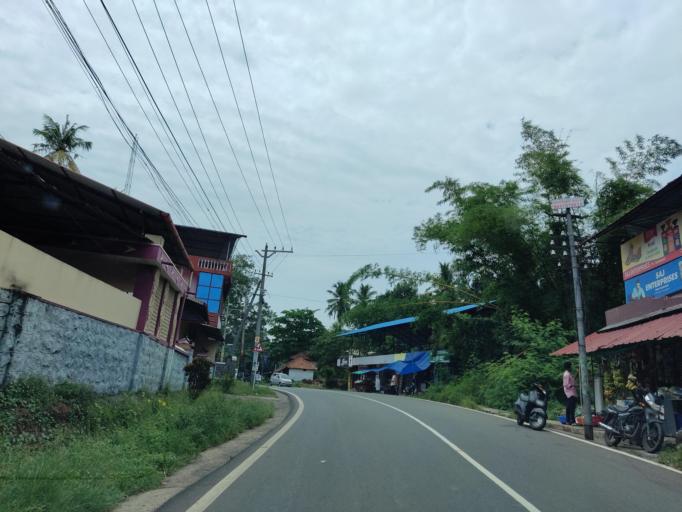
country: IN
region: Kerala
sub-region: Alappuzha
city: Chengannur
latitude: 9.2716
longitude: 76.6130
